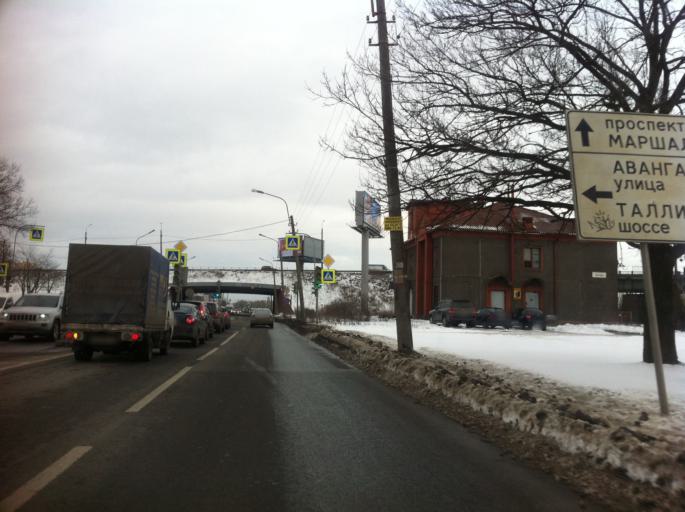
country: RU
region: St.-Petersburg
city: Uritsk
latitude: 59.8239
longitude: 30.1820
